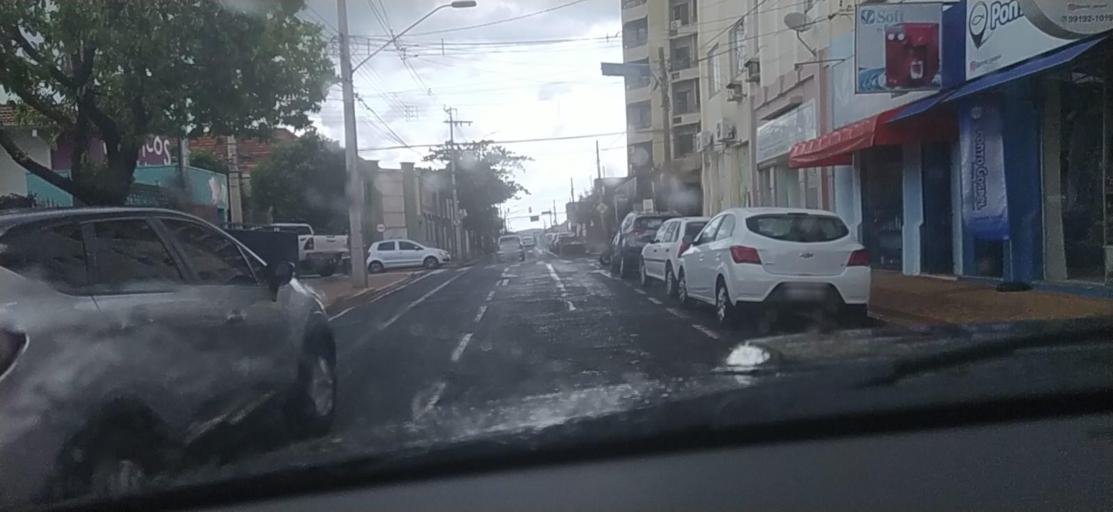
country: BR
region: Sao Paulo
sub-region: Catanduva
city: Catanduva
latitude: -21.1402
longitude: -48.9732
